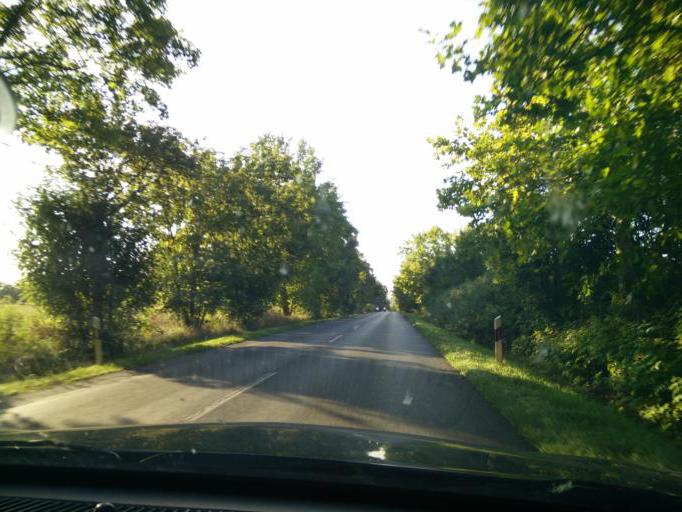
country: HU
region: Pest
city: Zsambek
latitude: 47.5283
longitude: 18.7365
